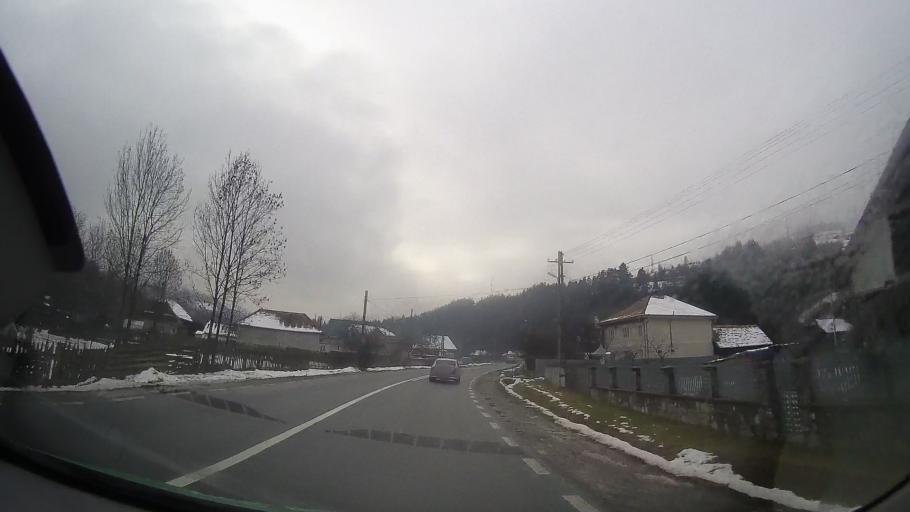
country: RO
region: Neamt
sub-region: Comuna Bicazu Ardelean
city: Bicazu Ardelean
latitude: 46.8640
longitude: 25.9398
